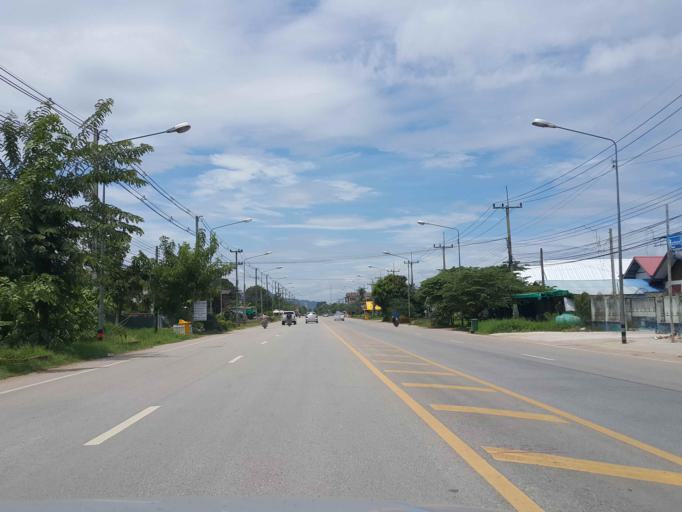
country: TH
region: Sukhothai
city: Ban Na
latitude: 17.0134
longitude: 99.7615
